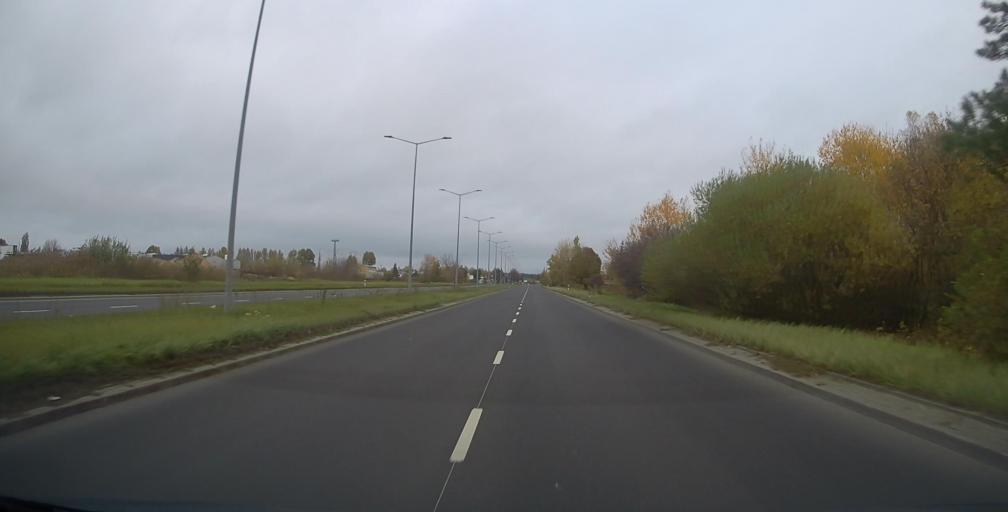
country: PL
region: Warmian-Masurian Voivodeship
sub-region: Powiat elcki
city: Elk
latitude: 53.8216
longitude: 22.3897
